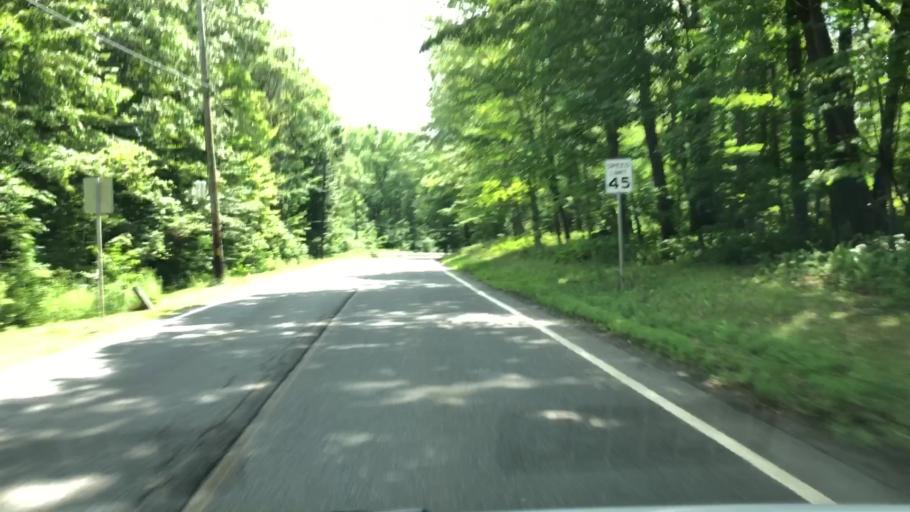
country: US
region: Massachusetts
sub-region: Hampshire County
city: Chesterfield
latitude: 42.4321
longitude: -72.7907
